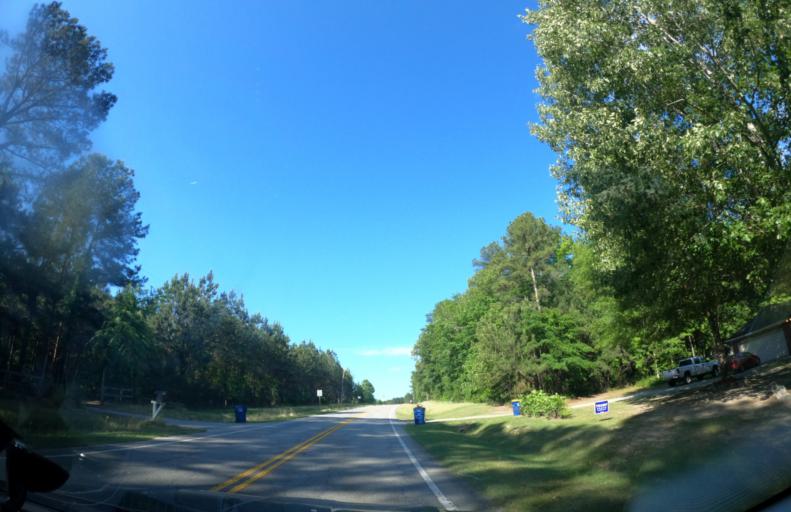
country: US
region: Georgia
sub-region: Columbia County
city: Harlem
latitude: 33.4282
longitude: -82.2954
